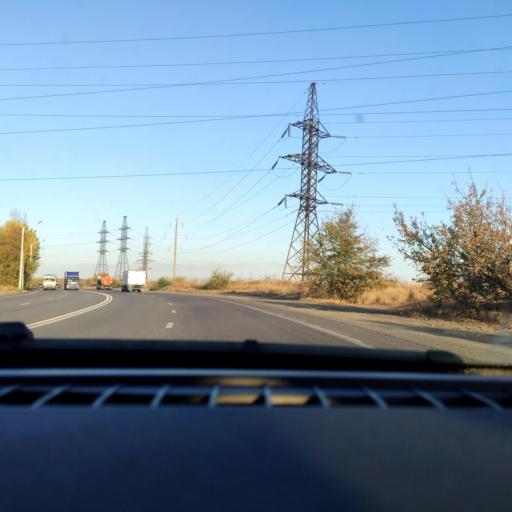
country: RU
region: Voronezj
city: Maslovka
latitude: 51.6209
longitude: 39.2736
